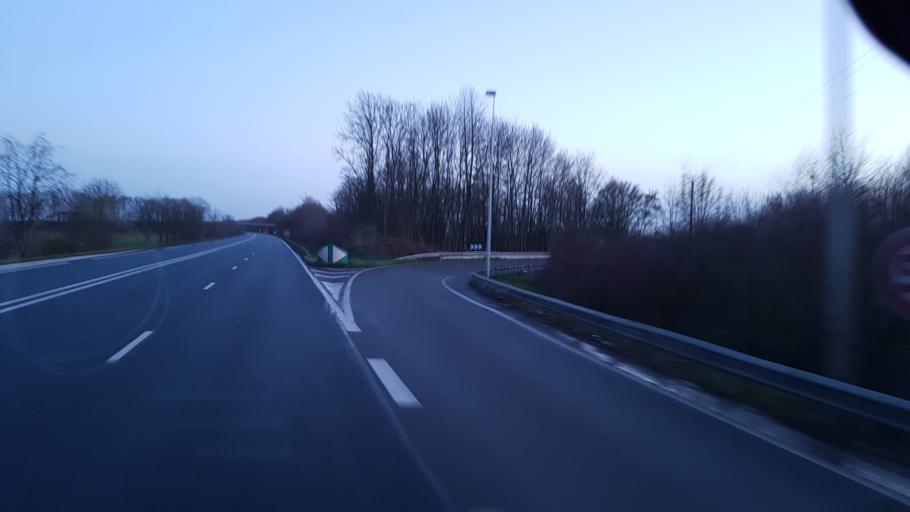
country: FR
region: Nord-Pas-de-Calais
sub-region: Departement du Nord
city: Ferin
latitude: 50.3352
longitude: 3.0902
